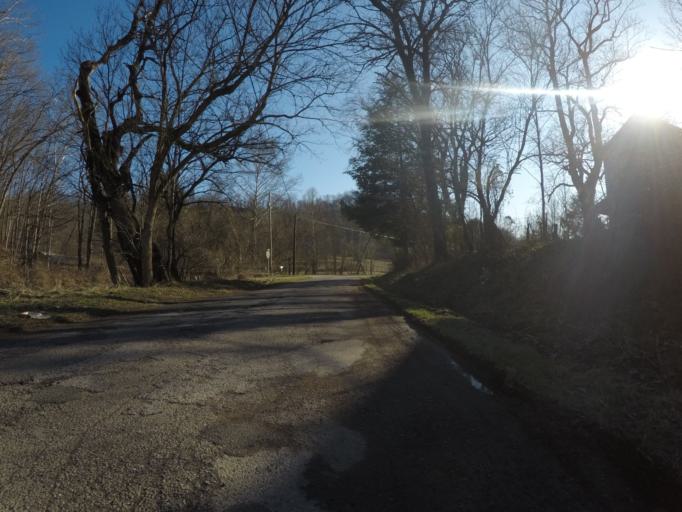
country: US
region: West Virginia
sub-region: Cabell County
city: Huntington
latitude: 38.5067
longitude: -82.4490
